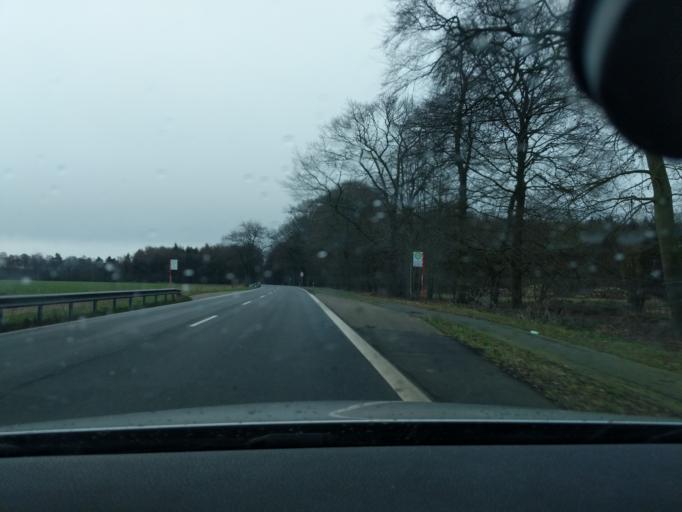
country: DE
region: Lower Saxony
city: Oldendorf
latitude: 53.5369
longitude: 9.2726
